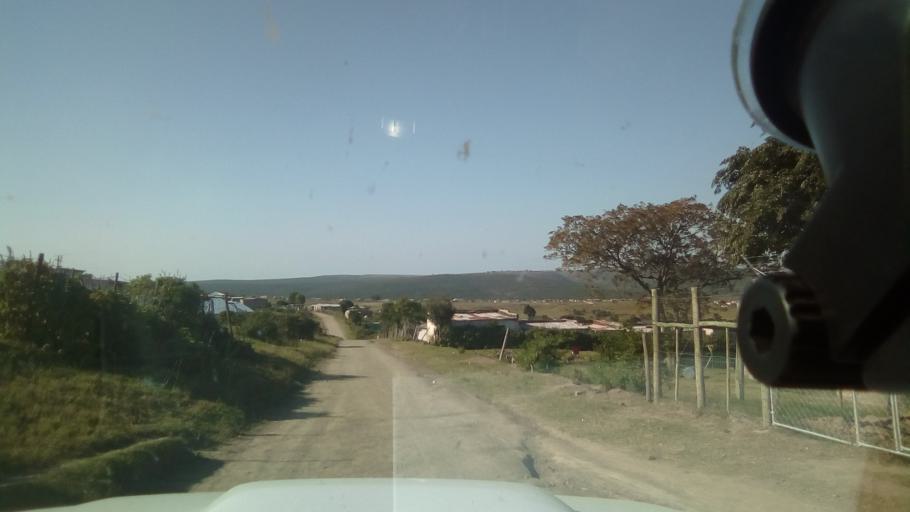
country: ZA
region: Eastern Cape
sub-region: Buffalo City Metropolitan Municipality
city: Bhisho
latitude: -32.8129
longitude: 27.3514
